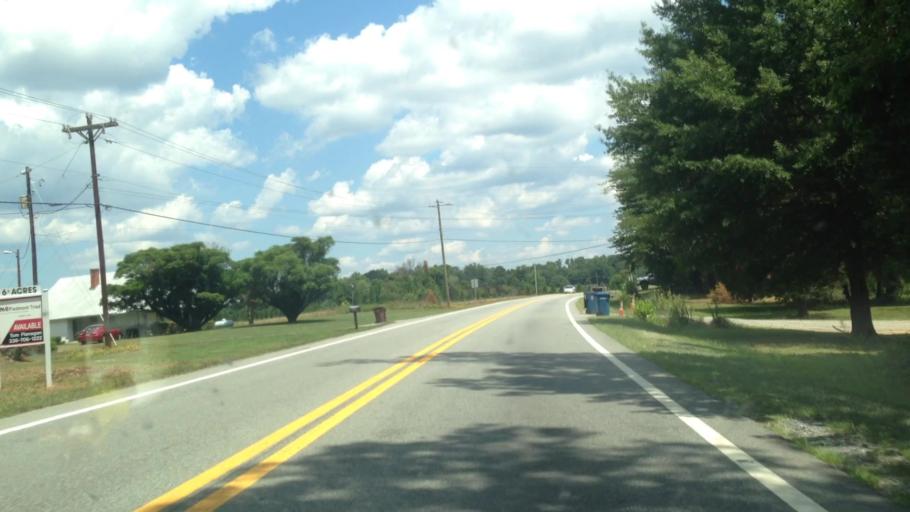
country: US
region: North Carolina
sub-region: Guilford County
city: Stokesdale
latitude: 36.2177
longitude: -79.9914
